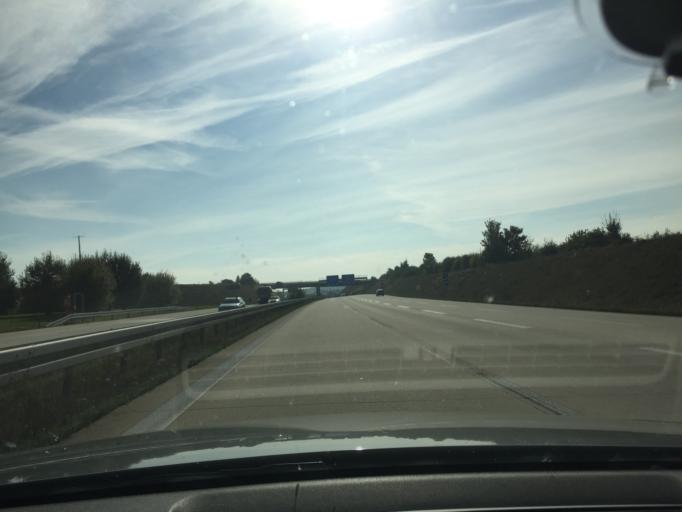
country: DE
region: Saxony
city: Dohna
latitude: 50.9507
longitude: 13.8718
